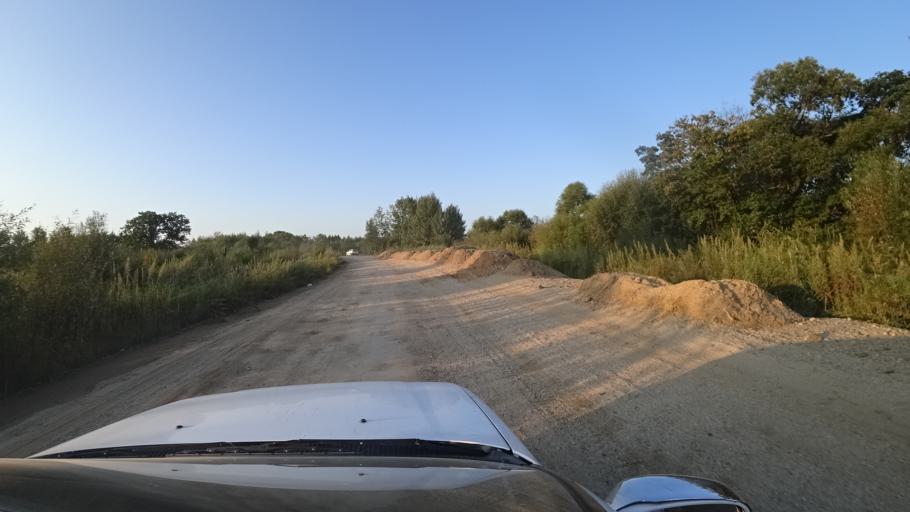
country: RU
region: Primorskiy
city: Dal'nerechensk
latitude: 45.9407
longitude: 133.7610
